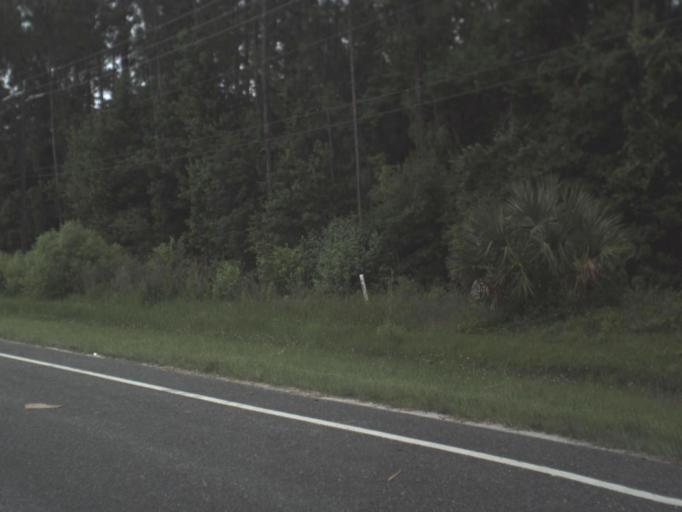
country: US
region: Florida
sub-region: Putnam County
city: Palatka
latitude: 29.6757
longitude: -81.6591
